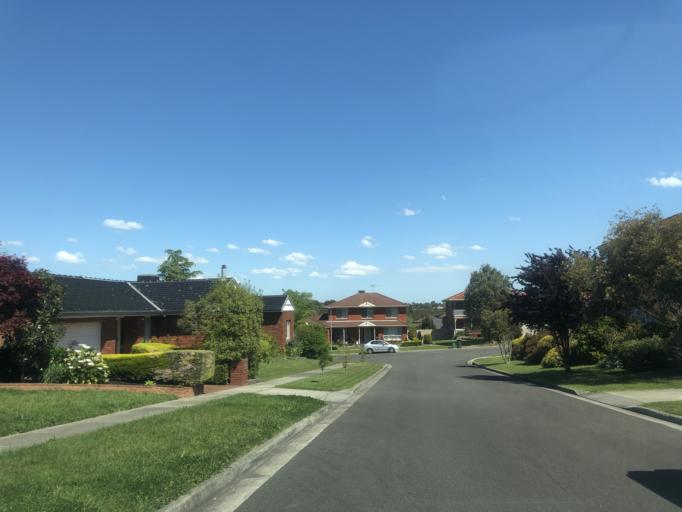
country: AU
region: Victoria
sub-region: Casey
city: Endeavour Hills
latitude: -37.9887
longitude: 145.2692
